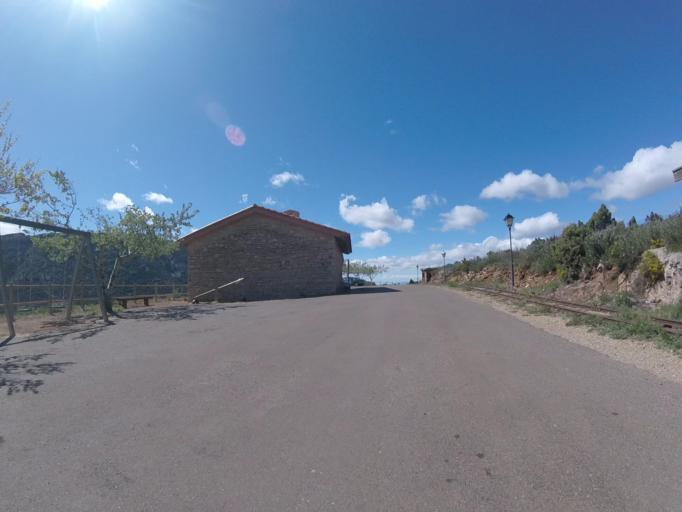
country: ES
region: Valencia
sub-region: Provincia de Castello
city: Culla
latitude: 40.3100
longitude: -0.0981
